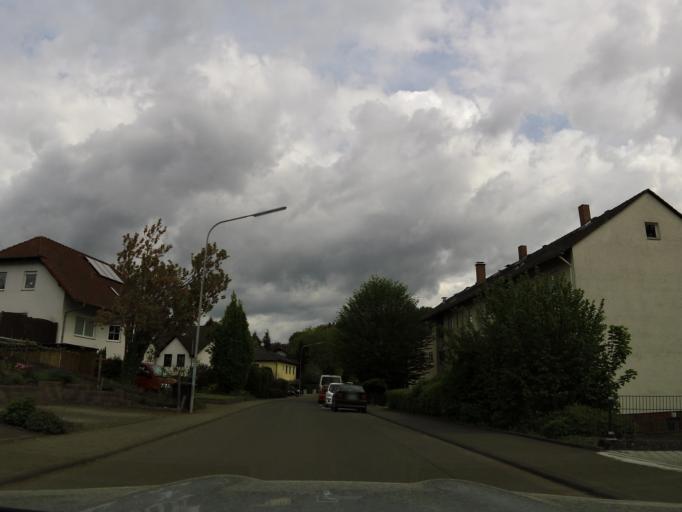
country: DE
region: Hesse
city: Oberbiel
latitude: 50.5571
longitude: 8.4371
